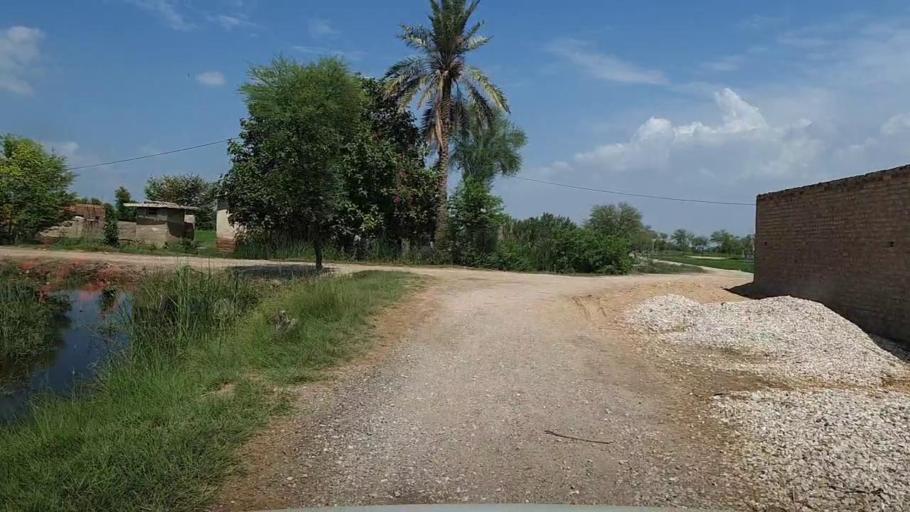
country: PK
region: Sindh
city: Bhiria
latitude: 26.9451
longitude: 68.2438
